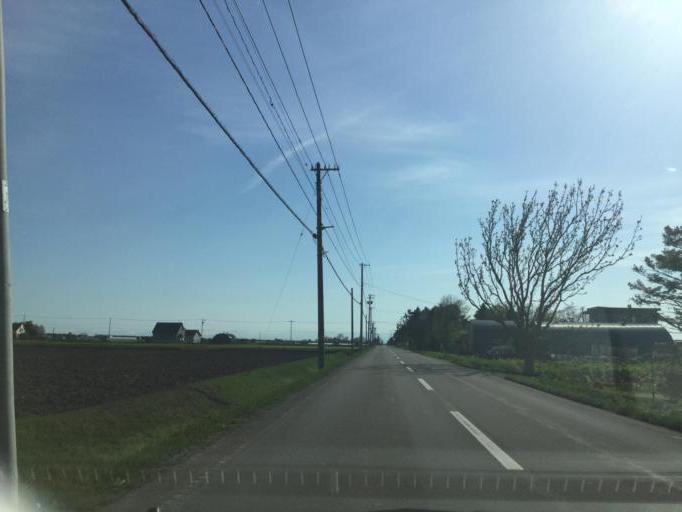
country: JP
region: Hokkaido
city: Iwamizawa
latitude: 43.1715
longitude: 141.7438
